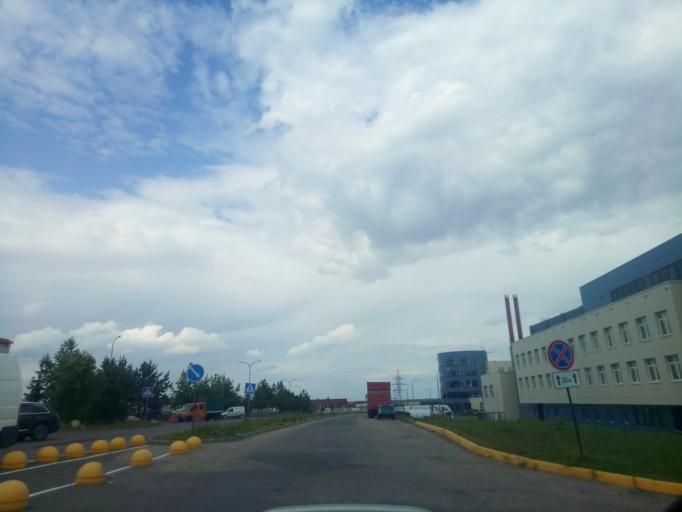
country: BY
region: Minsk
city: Zhdanovichy
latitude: 53.9359
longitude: 27.4220
